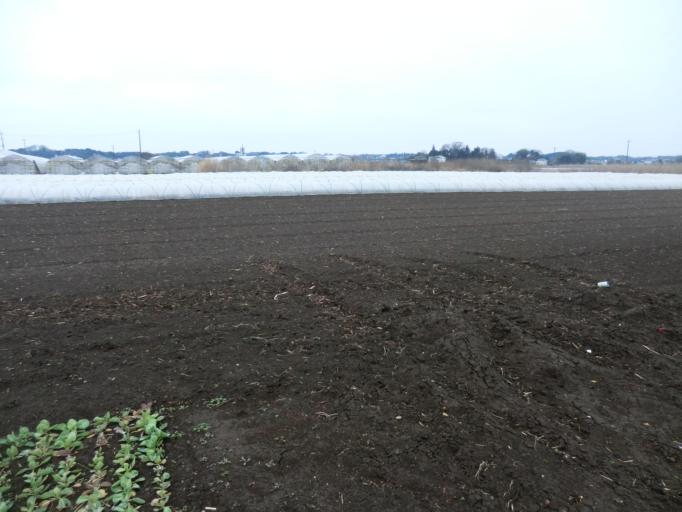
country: JP
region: Ibaraki
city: Naka
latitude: 36.0958
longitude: 140.1545
